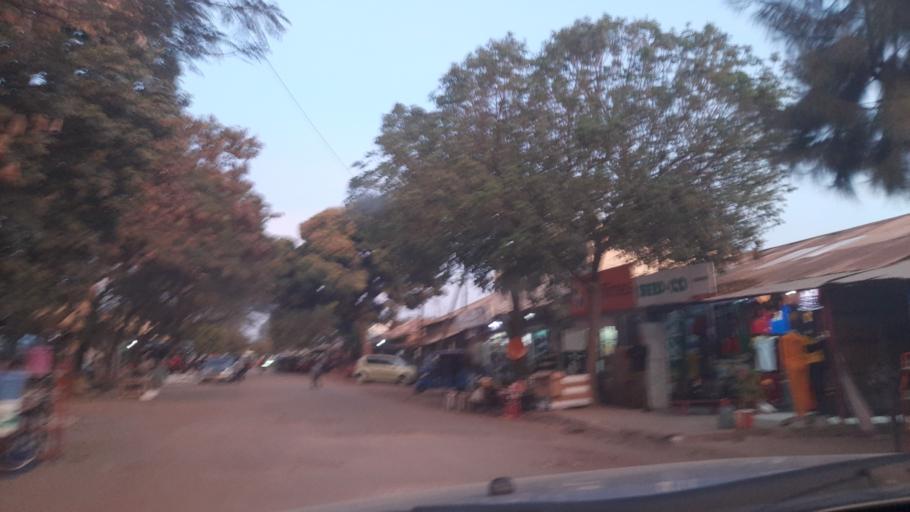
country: TZ
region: Singida
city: Singida
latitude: -4.8167
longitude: 34.7494
